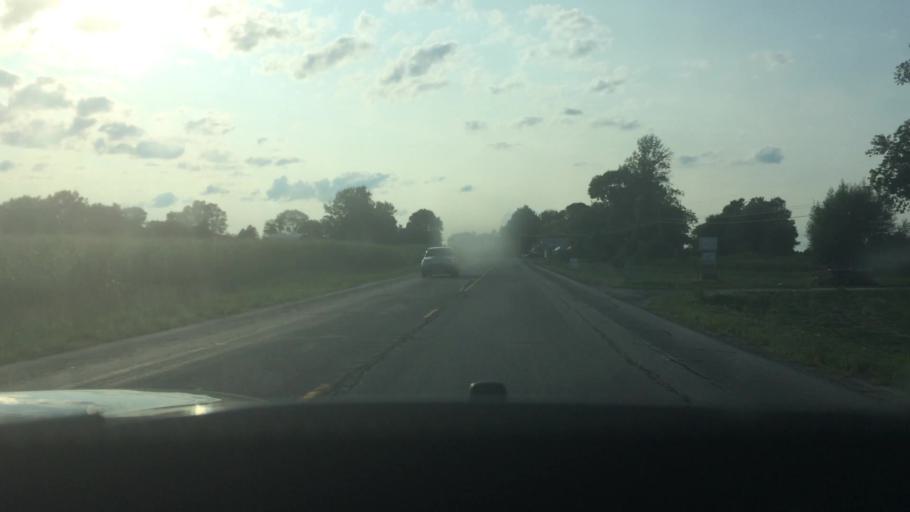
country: US
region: New York
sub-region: St. Lawrence County
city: Ogdensburg
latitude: 44.6703
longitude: -75.3820
